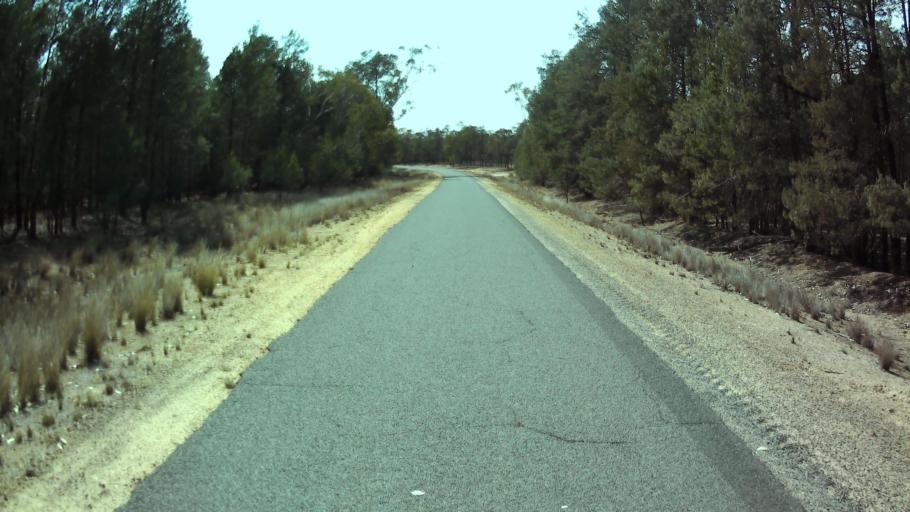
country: AU
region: New South Wales
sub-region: Weddin
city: Grenfell
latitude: -33.7495
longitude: 148.0593
